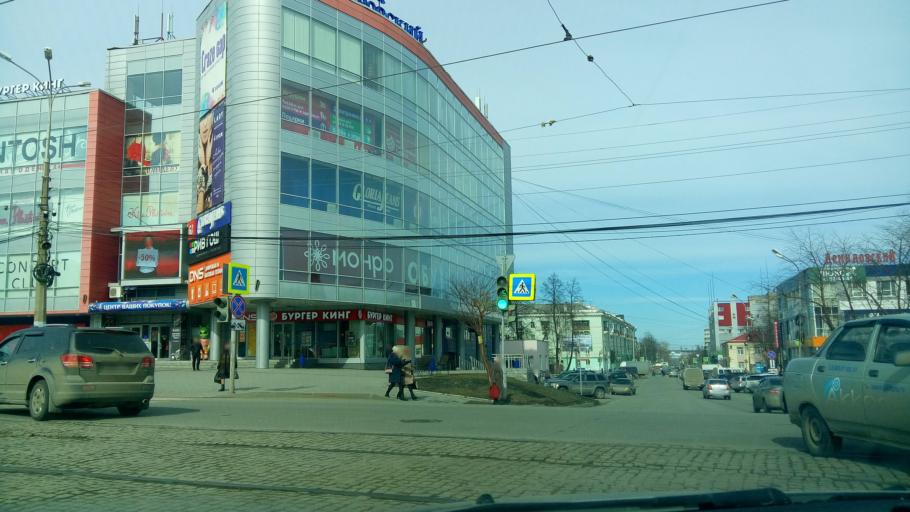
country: RU
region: Sverdlovsk
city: Nizhniy Tagil
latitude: 57.9077
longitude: 59.9603
